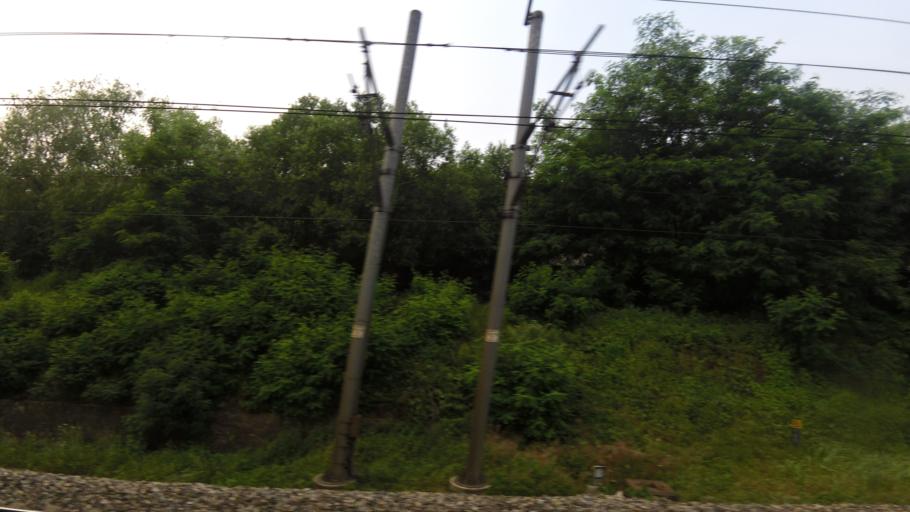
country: KR
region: Daejeon
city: Sintansin
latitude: 36.5311
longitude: 127.3713
